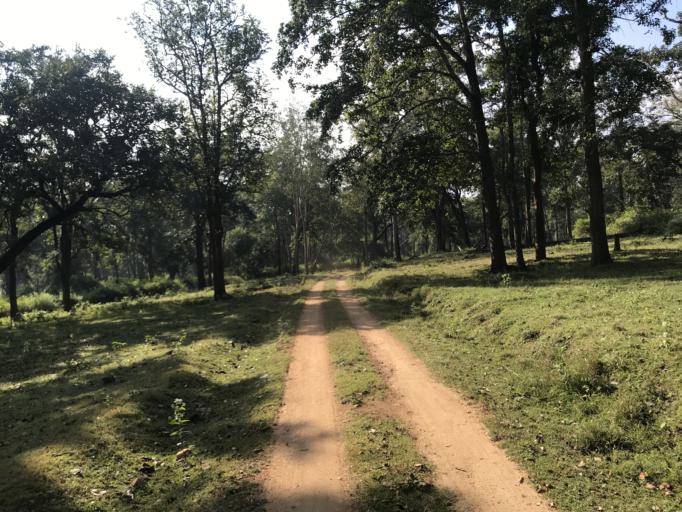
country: IN
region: Karnataka
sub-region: Mysore
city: Heggadadevankote
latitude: 11.9481
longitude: 76.2188
